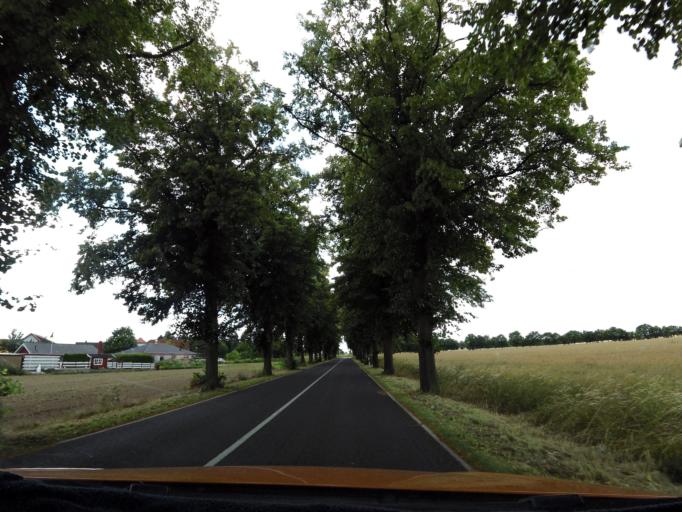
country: DE
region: Brandenburg
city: Mittenwalde
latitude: 52.2916
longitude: 13.5427
